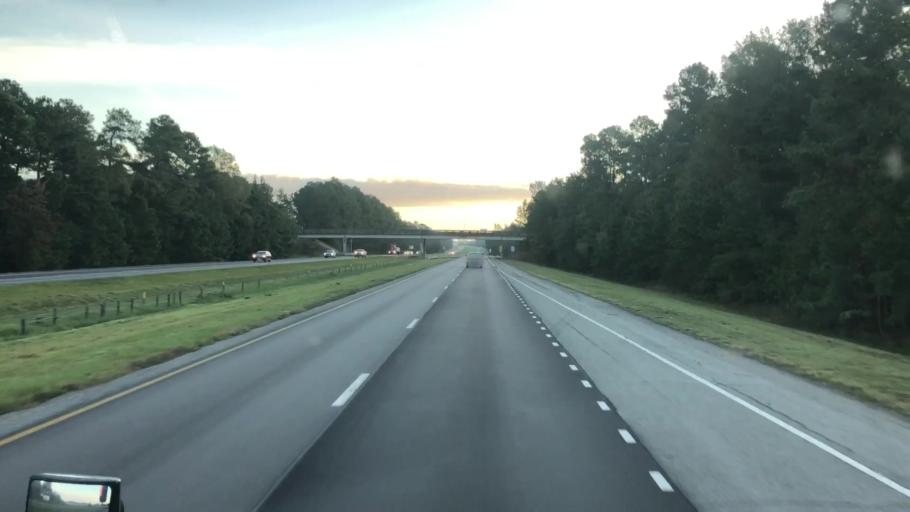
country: US
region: South Carolina
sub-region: Clarendon County
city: Manning
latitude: 33.5918
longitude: -80.3493
